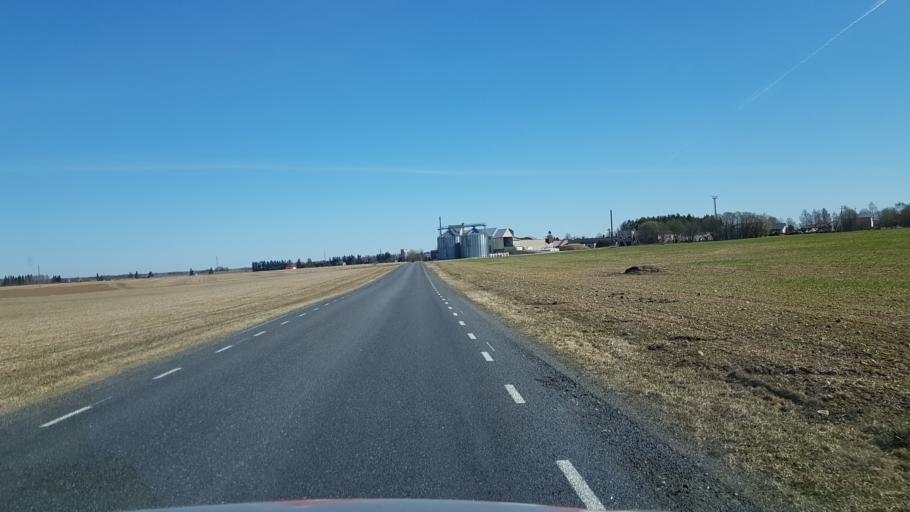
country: EE
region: Laeaene-Virumaa
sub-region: Vinni vald
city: Vinni
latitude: 59.2822
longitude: 26.3935
